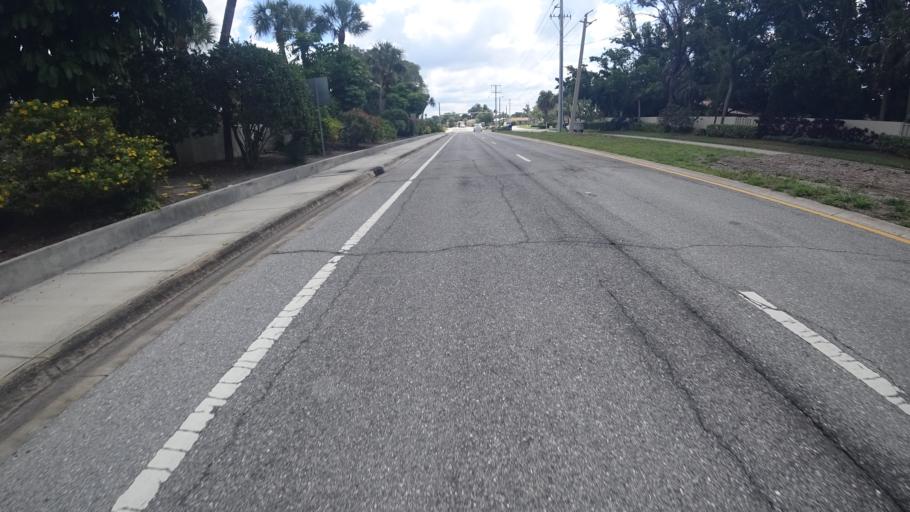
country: US
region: Florida
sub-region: Manatee County
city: Bayshore Gardens
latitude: 27.4294
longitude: -82.5974
